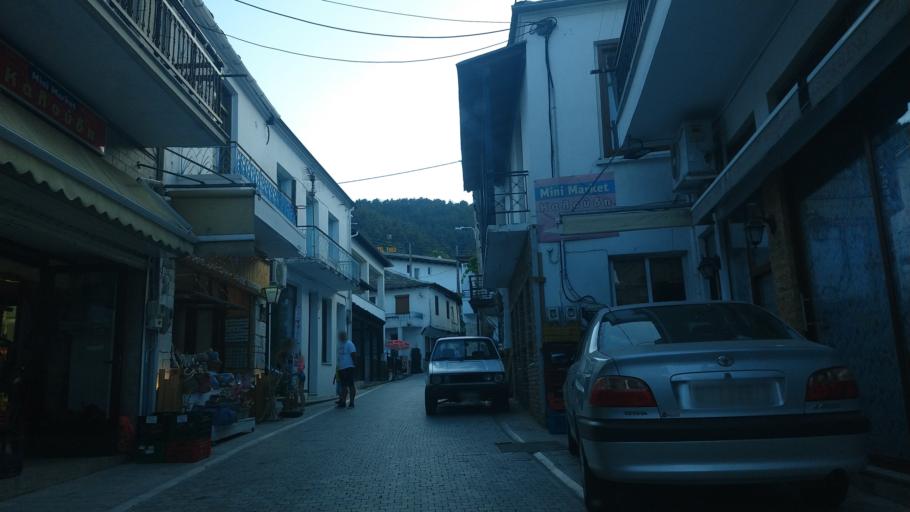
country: GR
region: East Macedonia and Thrace
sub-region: Nomos Kavalas
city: Potamia
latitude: 40.7313
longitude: 24.7289
